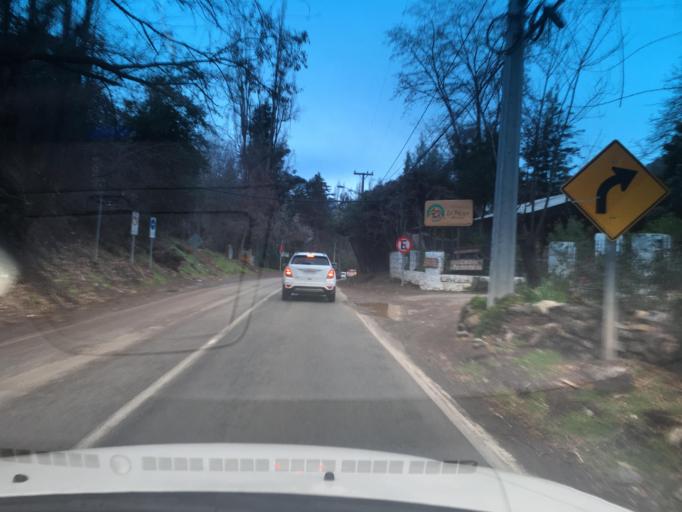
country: CL
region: Santiago Metropolitan
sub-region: Provincia de Cordillera
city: Puente Alto
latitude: -33.7244
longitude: -70.3227
